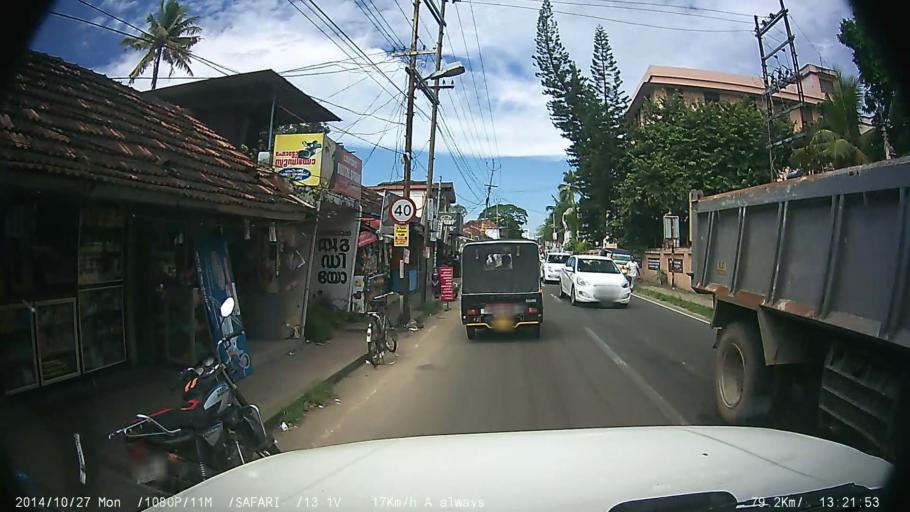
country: IN
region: Kerala
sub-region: Alappuzha
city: Alleppey
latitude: 9.4978
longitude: 76.3285
